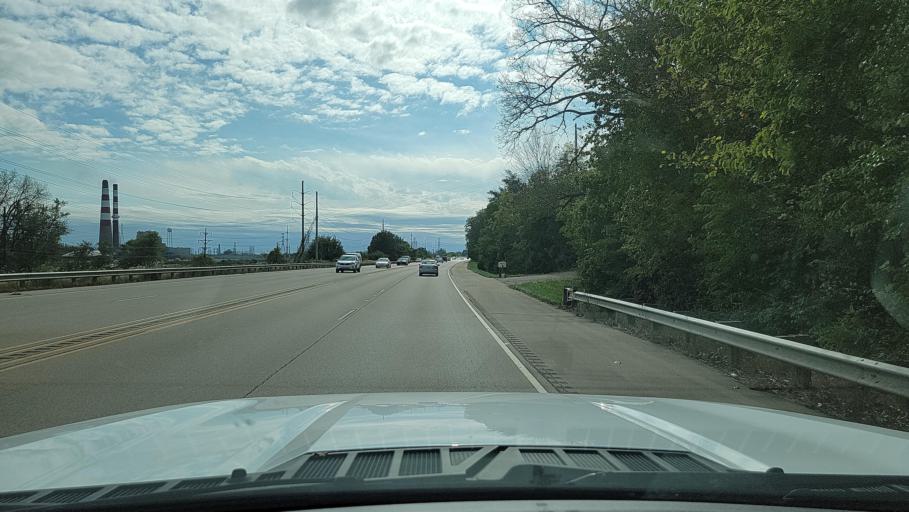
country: US
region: Illinois
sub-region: Tazewell County
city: North Pekin
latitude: 40.6090
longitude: -89.6611
